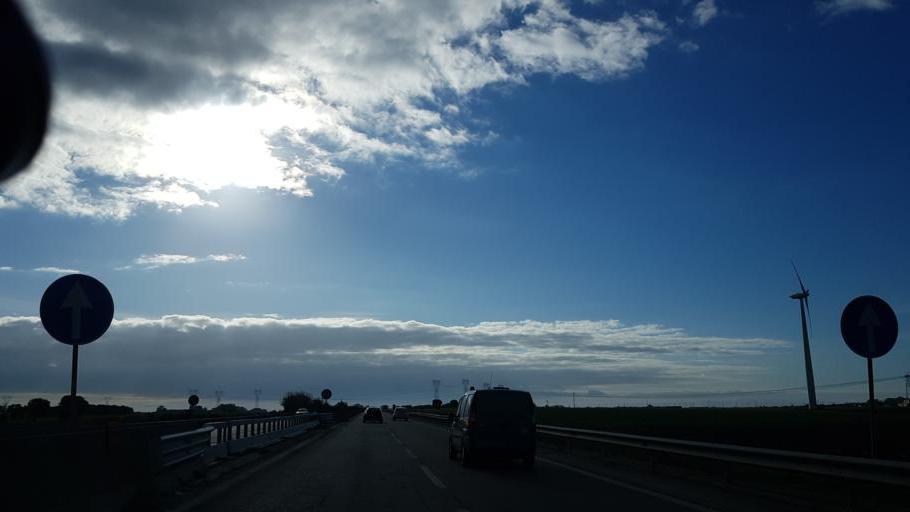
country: IT
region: Apulia
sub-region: Provincia di Brindisi
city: Tuturano
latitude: 40.5691
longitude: 17.9848
